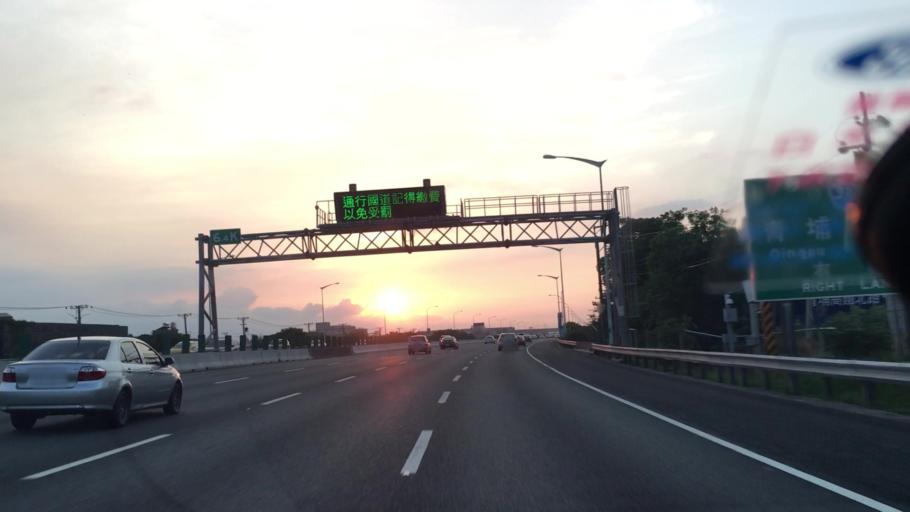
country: TW
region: Taiwan
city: Taoyuan City
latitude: 25.0284
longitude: 121.2516
